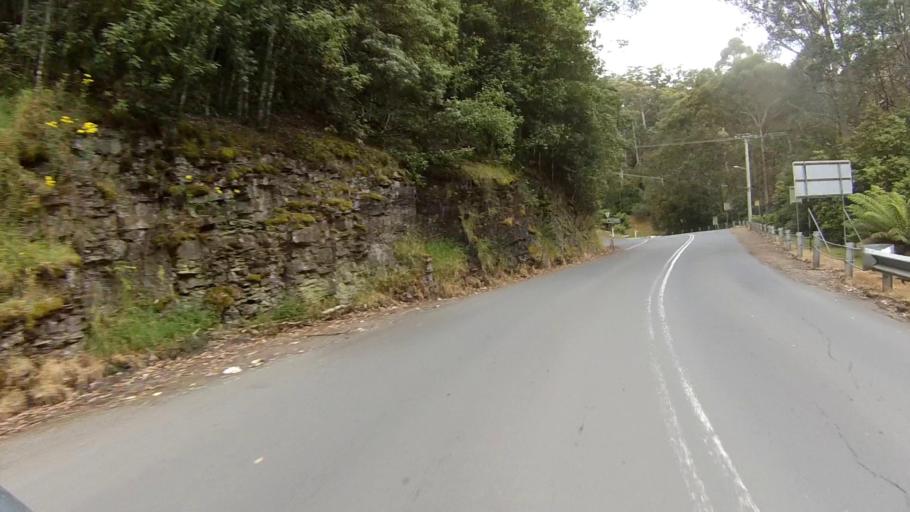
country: AU
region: Tasmania
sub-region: Hobart
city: Dynnyrne
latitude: -42.9208
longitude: 147.2597
